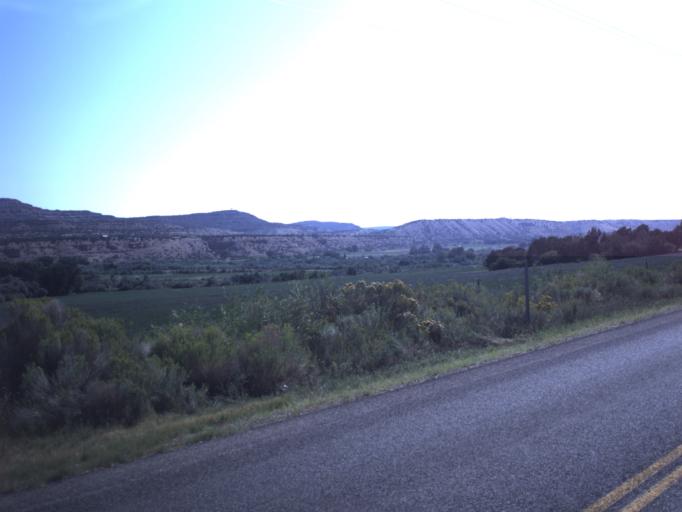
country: US
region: Utah
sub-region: Duchesne County
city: Duchesne
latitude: 40.2761
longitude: -110.4640
